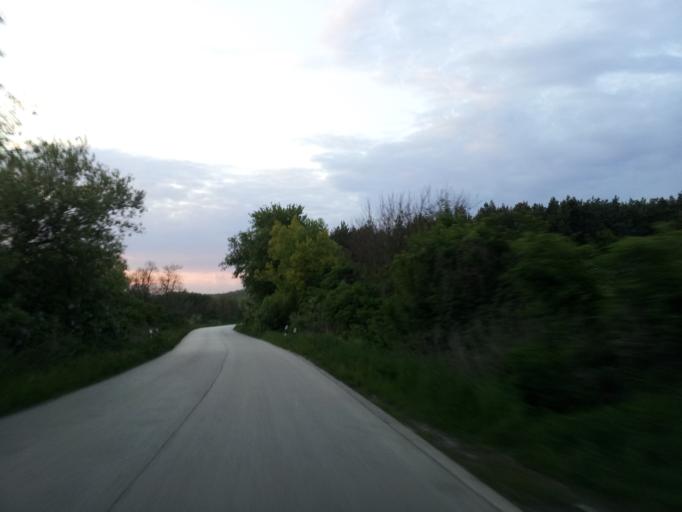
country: HU
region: Pest
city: Perbal
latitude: 47.6285
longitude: 18.7601
